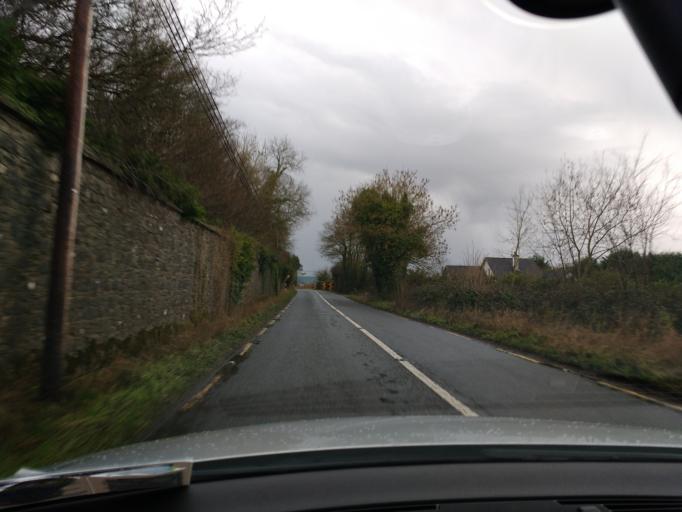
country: IE
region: Leinster
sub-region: Laois
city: Rathdowney
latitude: 52.6725
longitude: -7.5809
